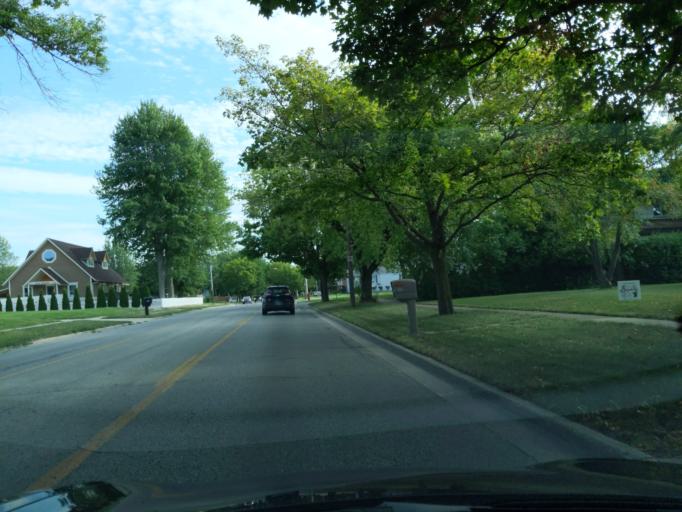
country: US
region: Michigan
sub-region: Midland County
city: Midland
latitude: 43.6451
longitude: -84.2269
